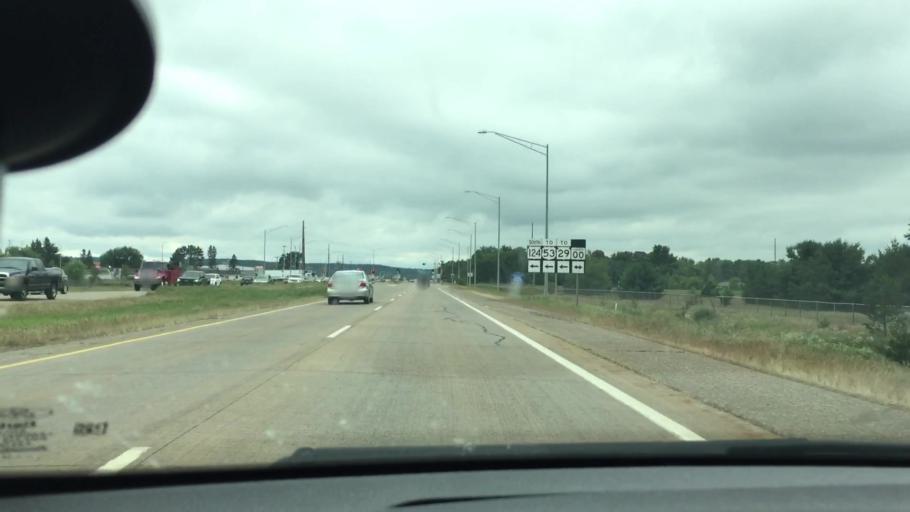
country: US
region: Wisconsin
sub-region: Chippewa County
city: Lake Hallie
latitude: 44.8895
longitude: -91.4218
